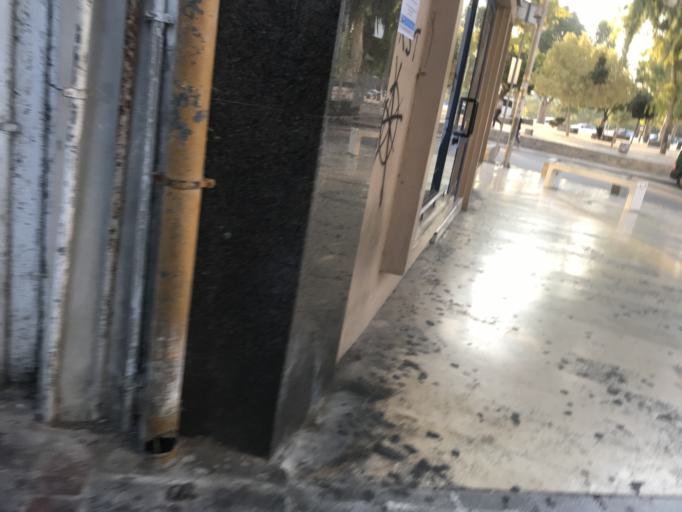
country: GR
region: Crete
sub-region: Nomos Irakleiou
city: Irakleion
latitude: 35.3384
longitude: 25.1361
